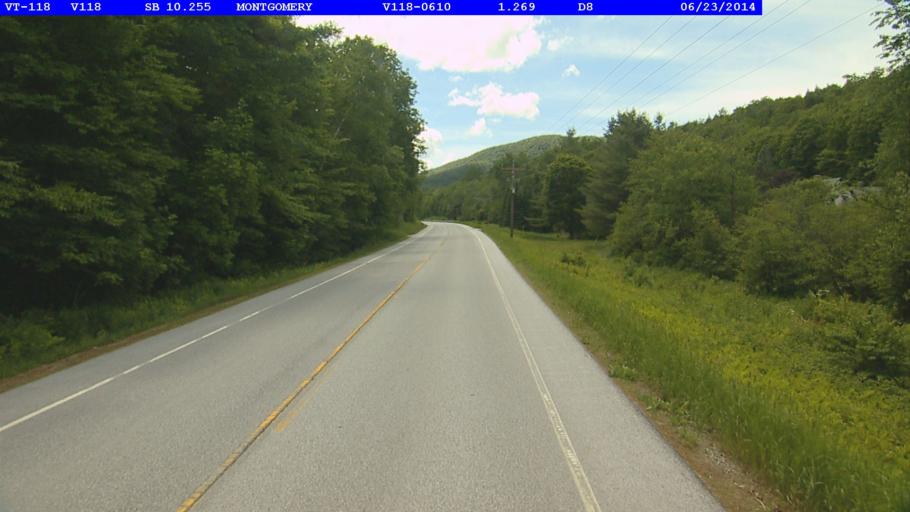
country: US
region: Vermont
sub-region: Franklin County
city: Richford
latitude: 44.8171
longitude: -72.6150
